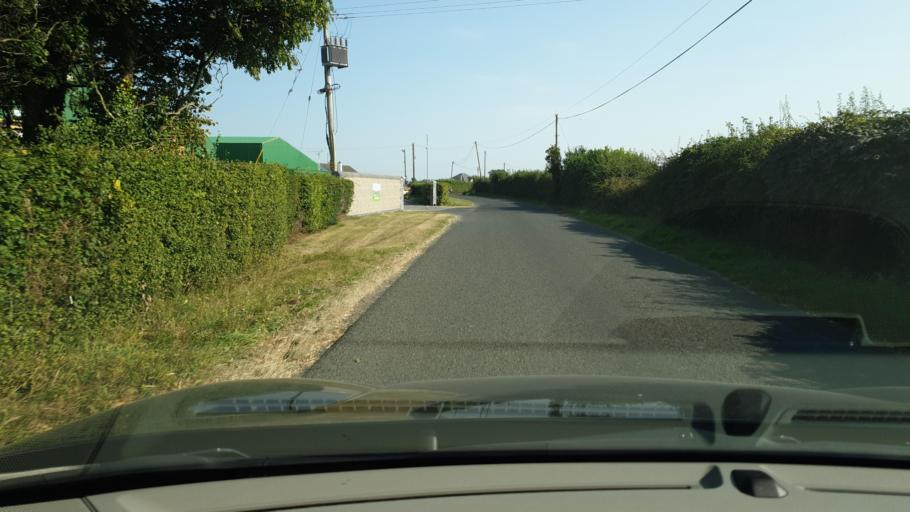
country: IE
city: Kentstown
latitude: 53.6135
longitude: -6.5067
